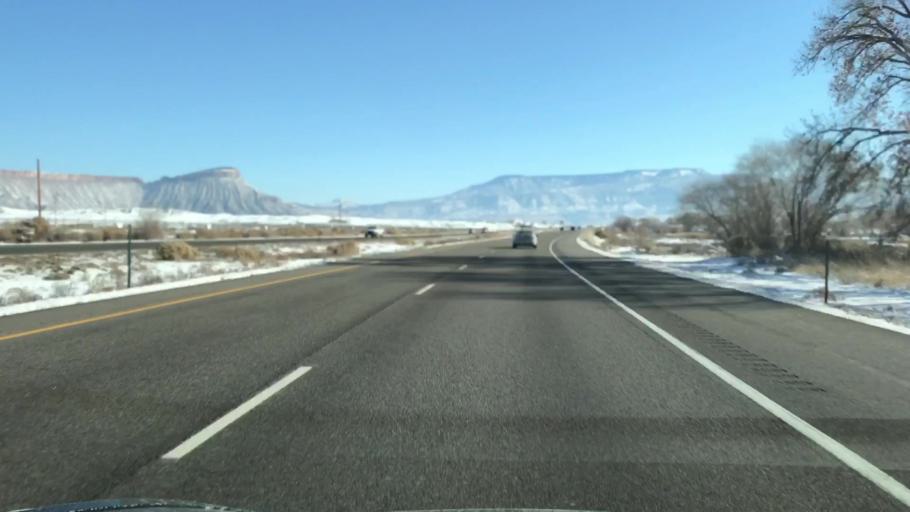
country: US
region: Colorado
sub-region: Mesa County
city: Fruitvale
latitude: 39.1086
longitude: -108.5038
